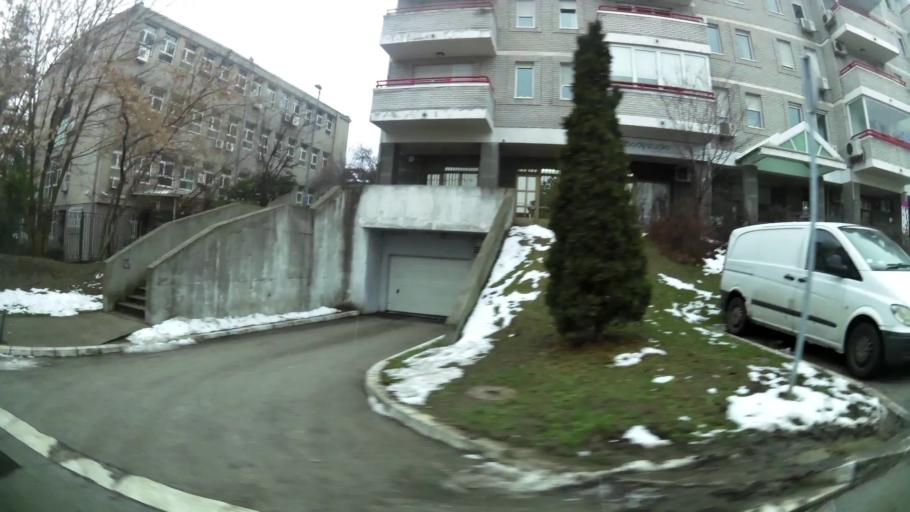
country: RS
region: Central Serbia
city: Belgrade
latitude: 44.7934
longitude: 20.4604
